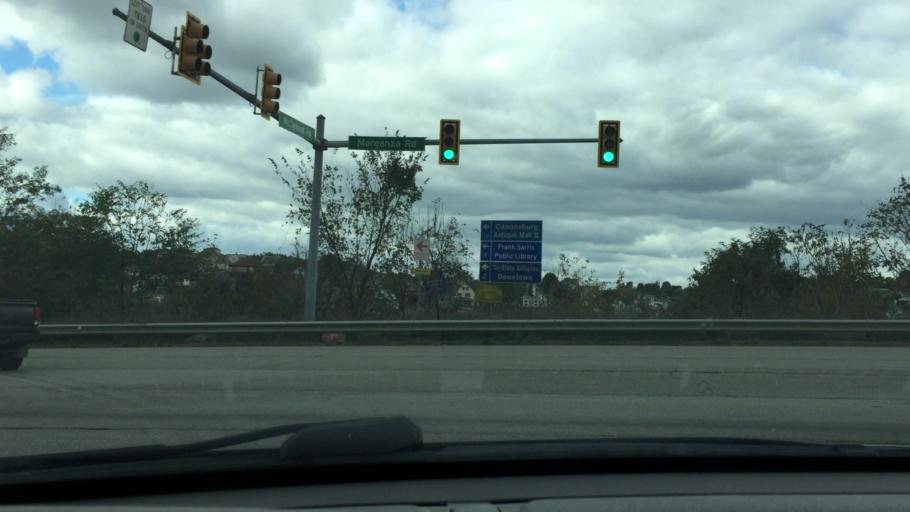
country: US
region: Pennsylvania
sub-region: Washington County
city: Canonsburg
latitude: 40.2642
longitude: -80.1708
